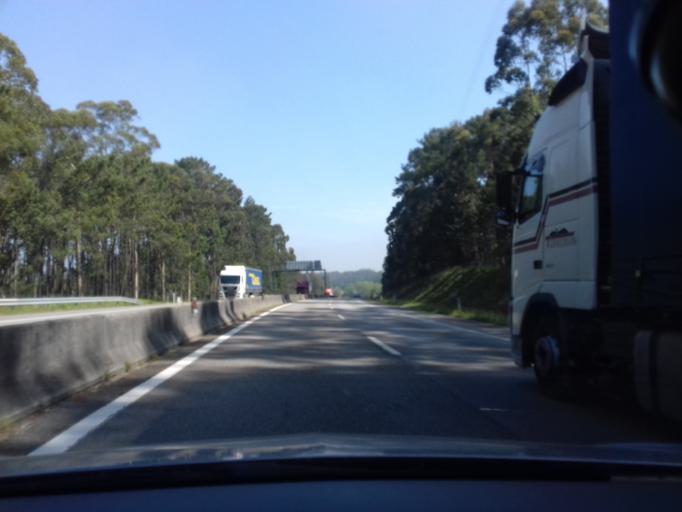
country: PT
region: Aveiro
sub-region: Ovar
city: Cortegaca
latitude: 40.9402
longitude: -8.6020
